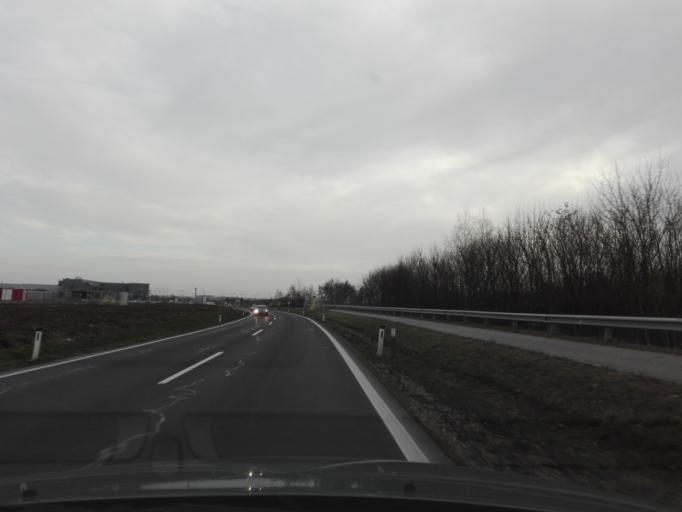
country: AT
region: Upper Austria
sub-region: Politischer Bezirk Linz-Land
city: Horsching
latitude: 48.2333
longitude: 14.1638
